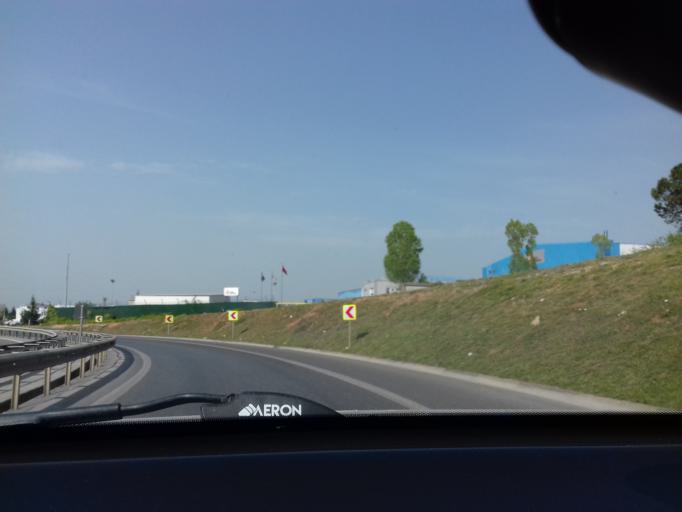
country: TR
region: Istanbul
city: Samandira
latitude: 40.9681
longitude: 29.2191
